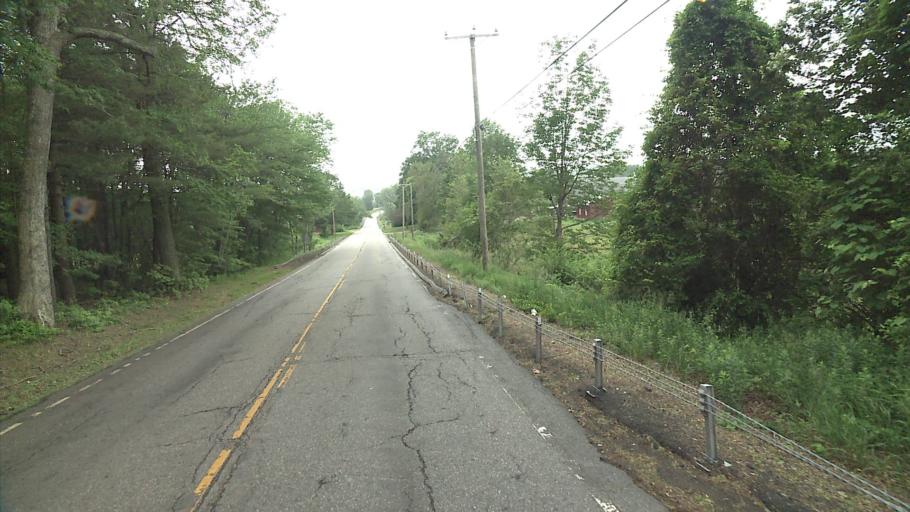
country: US
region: Connecticut
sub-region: Hartford County
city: Terramuggus
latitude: 41.6923
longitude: -72.4467
